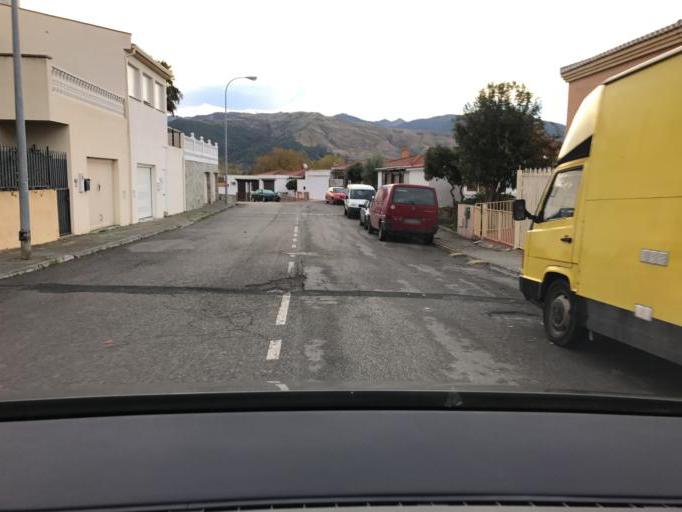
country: ES
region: Andalusia
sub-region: Provincia de Granada
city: Cenes de la Vega
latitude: 37.1680
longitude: -3.5456
